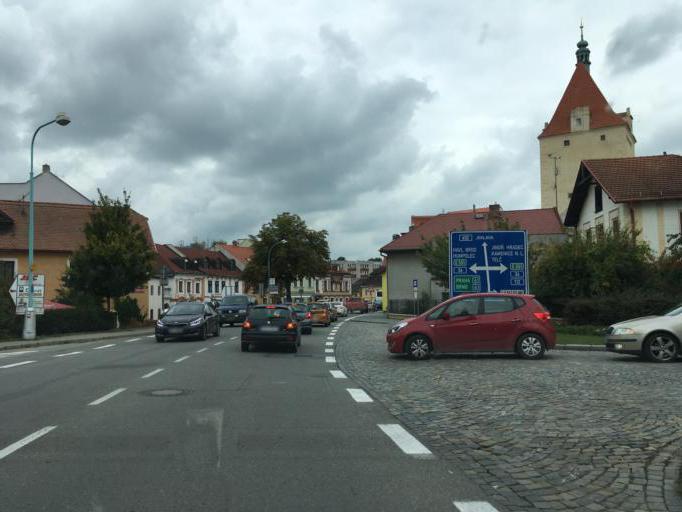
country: CZ
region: Vysocina
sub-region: Okres Pelhrimov
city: Pelhrimov
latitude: 49.4326
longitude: 15.2244
